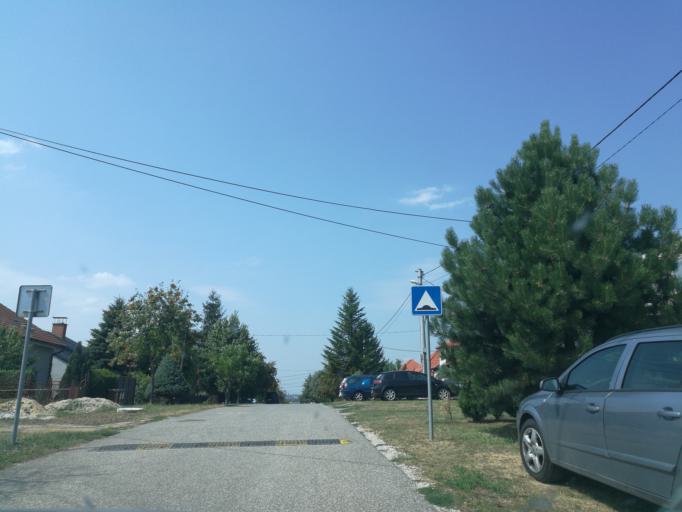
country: SK
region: Nitriansky
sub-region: Okres Nitra
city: Nitra
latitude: 48.2910
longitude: 18.1330
